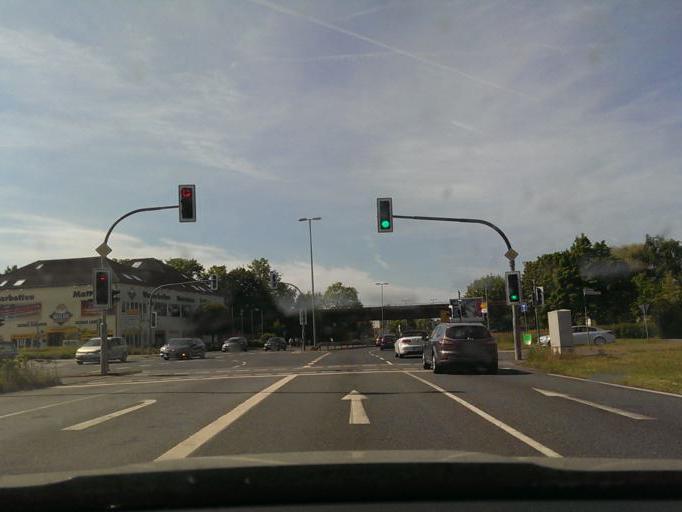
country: DE
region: Lower Saxony
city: Hildesheim
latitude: 52.1657
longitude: 9.9643
